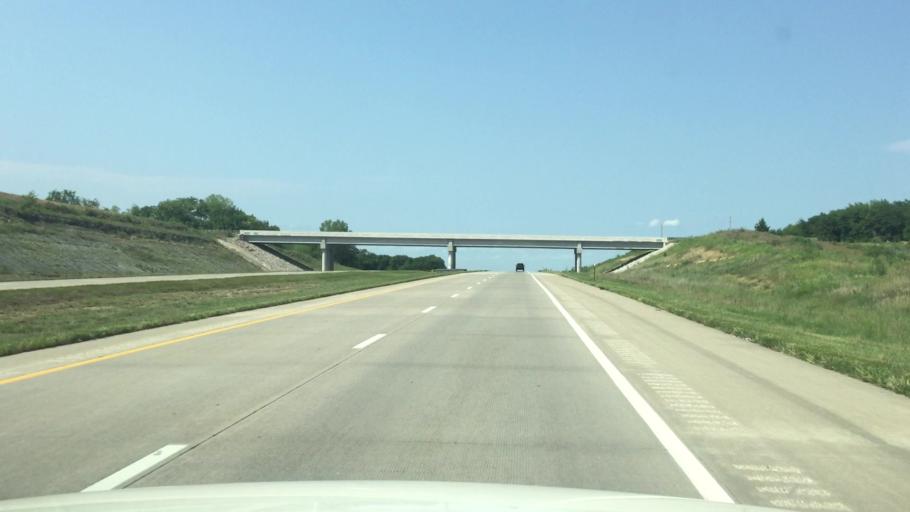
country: US
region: Kansas
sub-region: Linn County
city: Pleasanton
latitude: 38.1081
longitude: -94.7133
